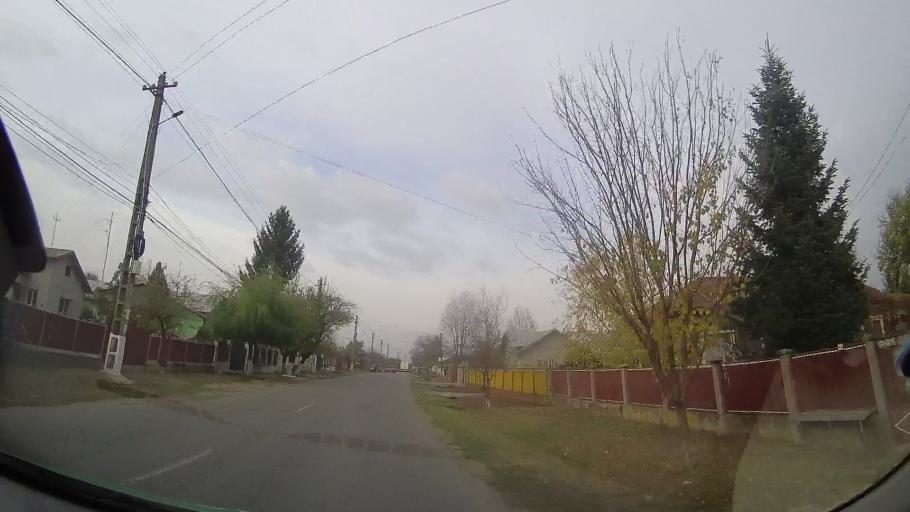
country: RO
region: Prahova
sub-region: Comuna Gorgota
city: Potigrafu
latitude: 44.7780
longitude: 26.1037
